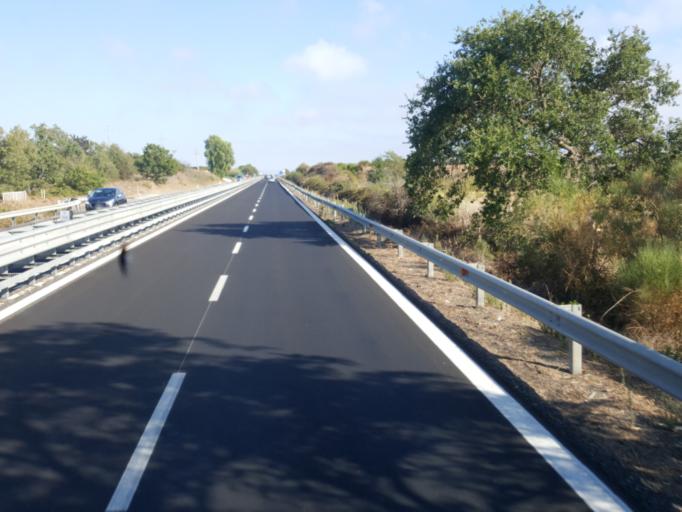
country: IT
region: Latium
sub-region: Provincia di Viterbo
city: Montalto di Castro
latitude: 42.3340
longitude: 11.6251
